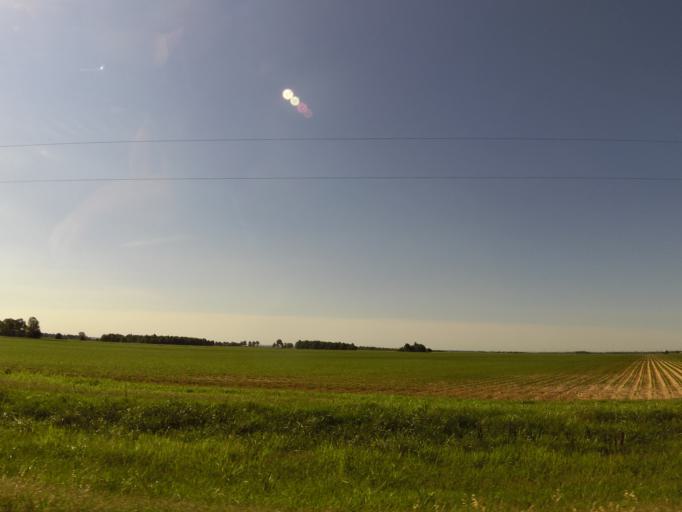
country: US
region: Arkansas
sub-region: Clay County
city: Corning
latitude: 36.4046
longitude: -90.5054
